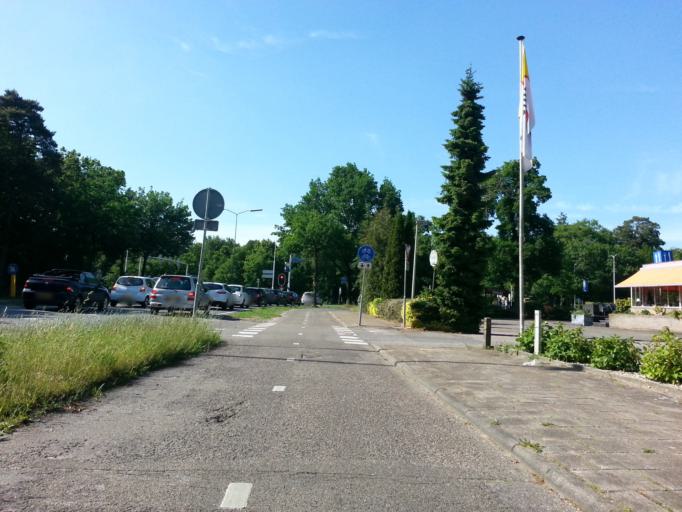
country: NL
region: Utrecht
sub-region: Gemeente Zeist
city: Zeist
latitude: 52.1071
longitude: 5.2371
